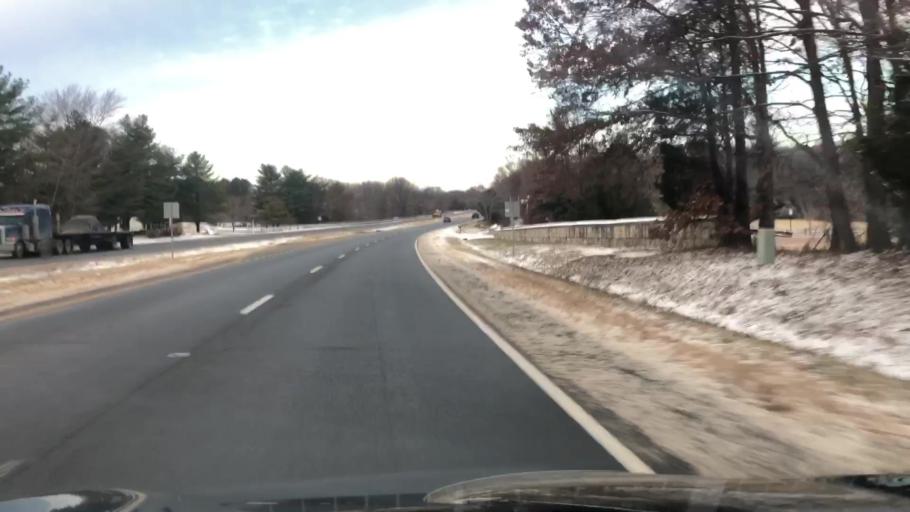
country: US
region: Virginia
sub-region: Fauquier County
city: Bealeton
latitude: 38.5642
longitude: -77.7530
